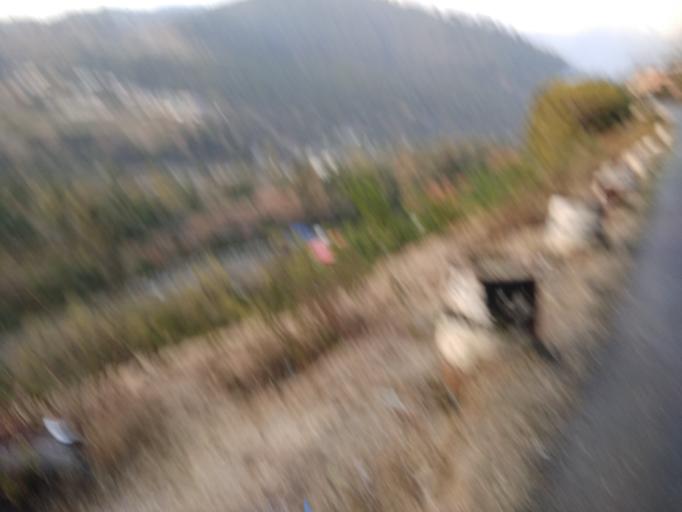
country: IN
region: Himachal Pradesh
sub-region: Kangra
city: Palampur
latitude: 32.1211
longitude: 76.5263
